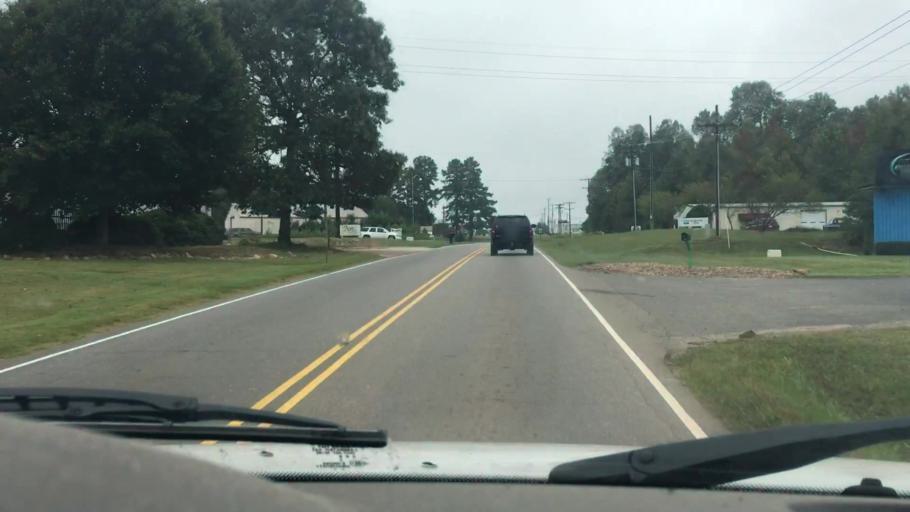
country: US
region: North Carolina
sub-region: Iredell County
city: Mooresville
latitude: 35.6039
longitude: -80.8090
